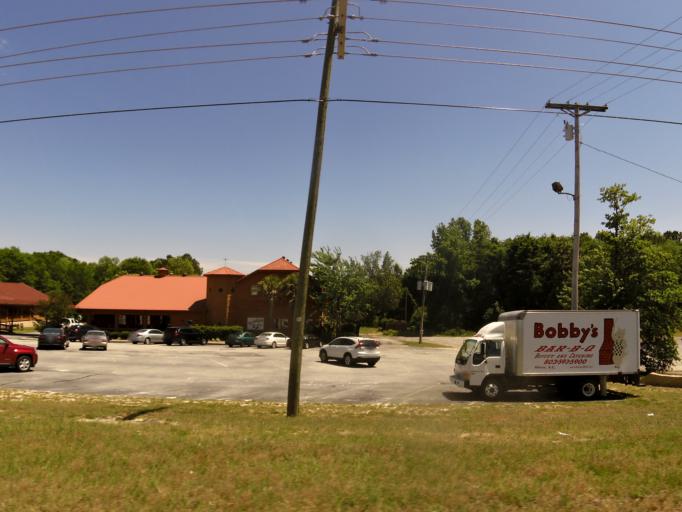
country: US
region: South Carolina
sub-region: Aiken County
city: Gloverville
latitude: 33.5397
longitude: -81.8307
